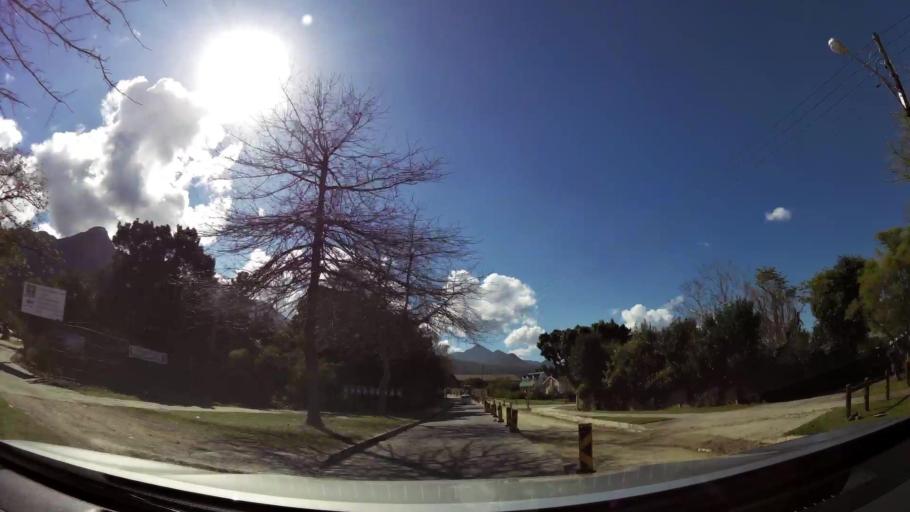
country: ZA
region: Western Cape
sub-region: Eden District Municipality
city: George
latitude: -33.9481
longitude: 22.4637
